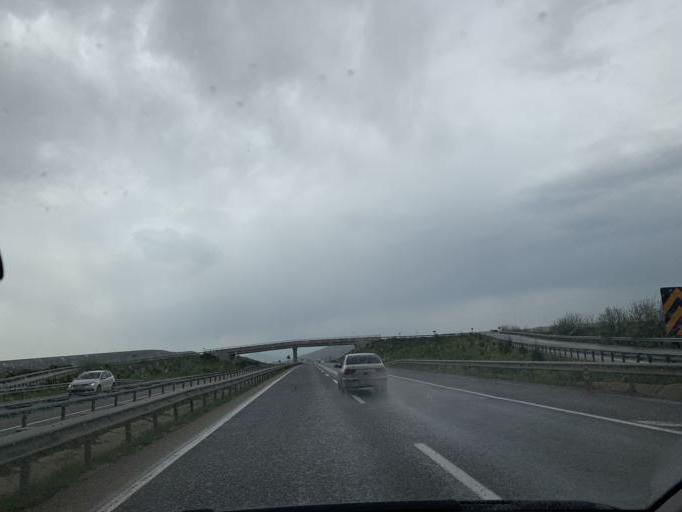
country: TR
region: Eskisehir
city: Gunyuzu
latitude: 39.5536
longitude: 31.7685
